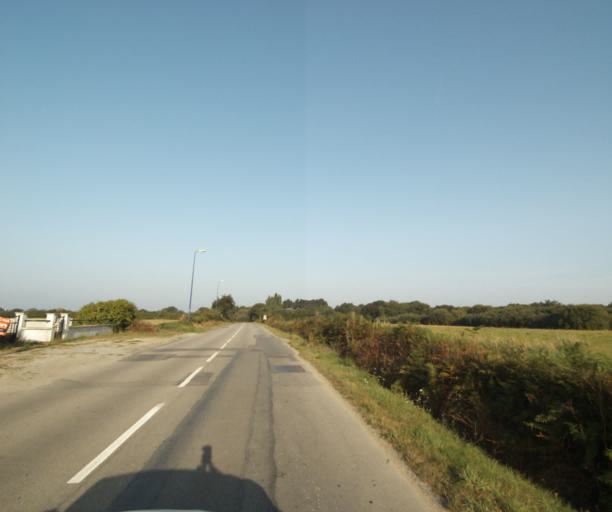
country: FR
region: Brittany
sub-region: Departement du Morbihan
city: Riantec
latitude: 47.7097
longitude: -3.2814
